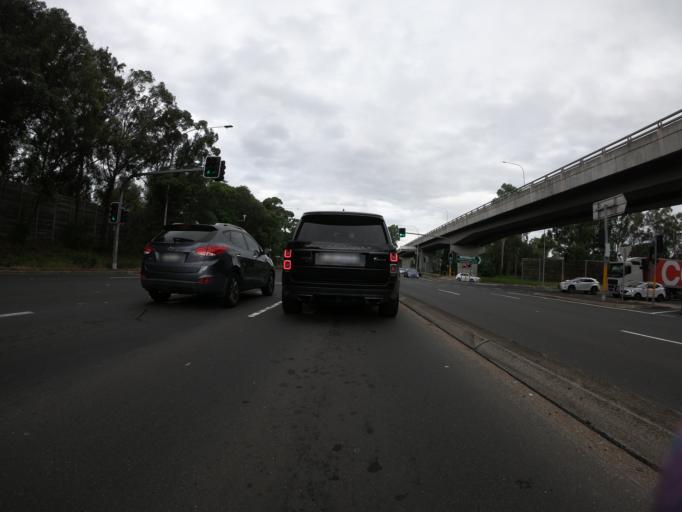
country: AU
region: New South Wales
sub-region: Parramatta
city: Constitution Hill
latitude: -33.7941
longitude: 150.9830
